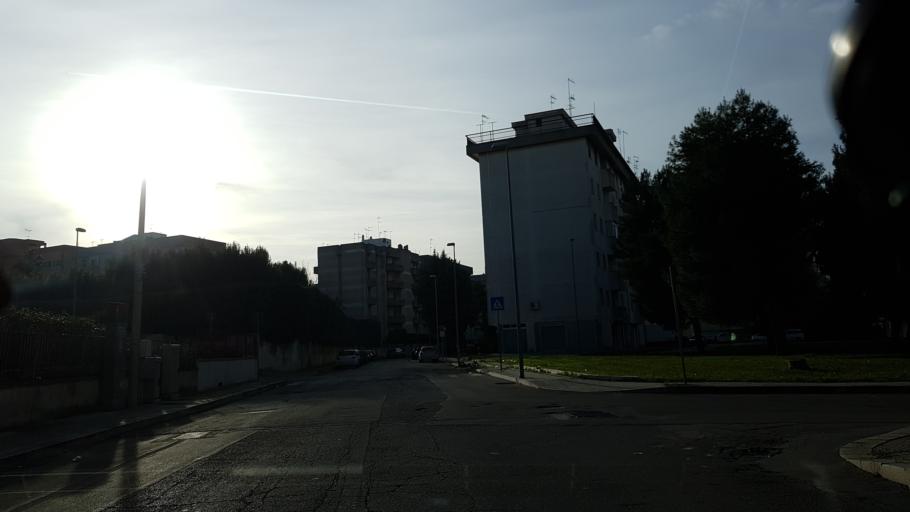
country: IT
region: Apulia
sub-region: Provincia di Brindisi
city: Brindisi
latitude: 40.6181
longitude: 17.9210
